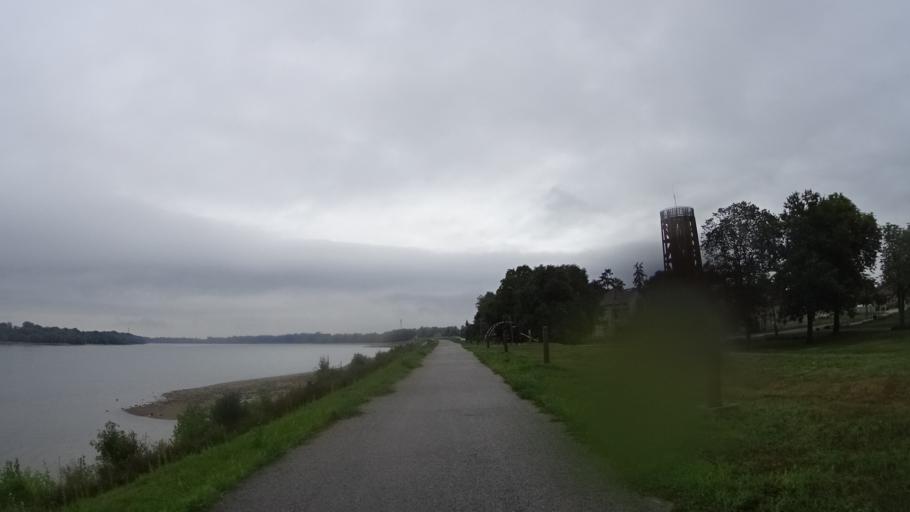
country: HU
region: Komarom-Esztergom
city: Labatlan
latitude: 47.7605
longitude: 18.4813
